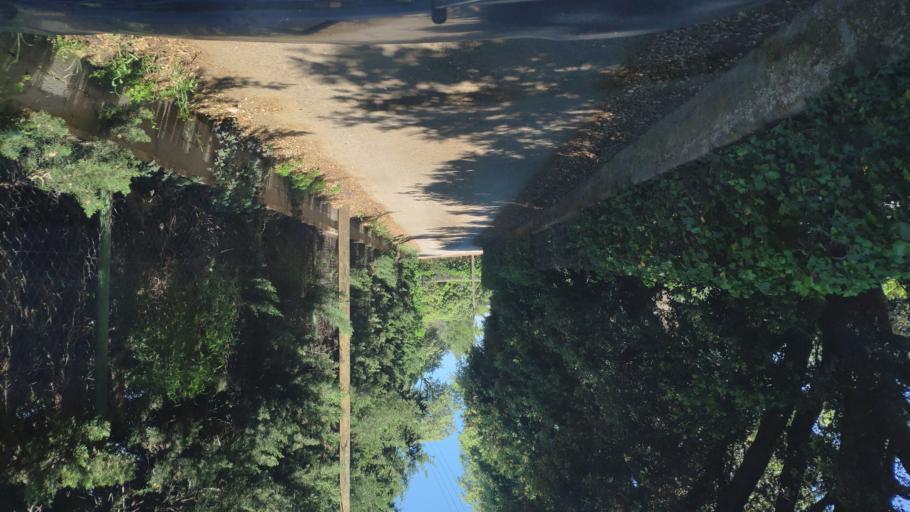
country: FR
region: Provence-Alpes-Cote d'Azur
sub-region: Departement du Vaucluse
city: Carpentras
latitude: 44.0795
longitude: 5.0496
